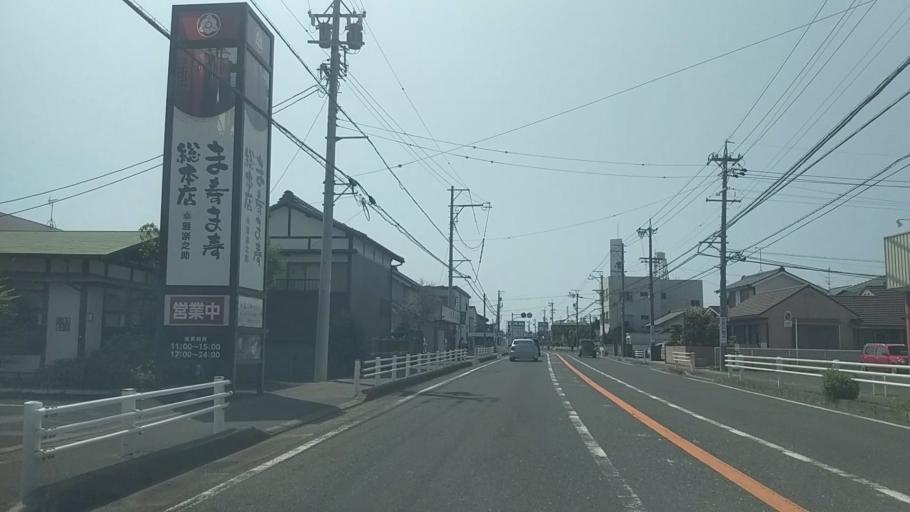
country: JP
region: Shizuoka
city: Hamamatsu
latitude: 34.6881
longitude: 137.7047
